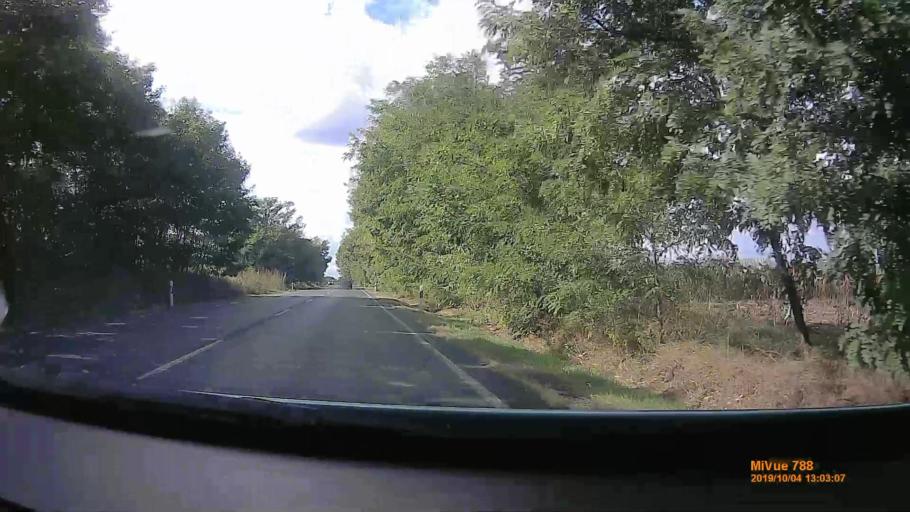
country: HU
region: Szabolcs-Szatmar-Bereg
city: Nyirtelek
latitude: 47.9578
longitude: 21.6401
